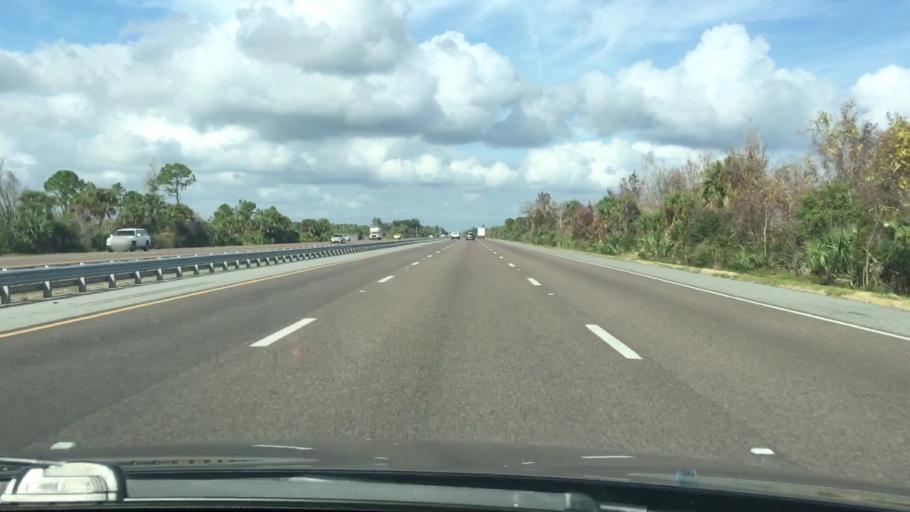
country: US
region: Florida
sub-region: Volusia County
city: Oak Hill
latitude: 28.7985
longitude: -80.9014
